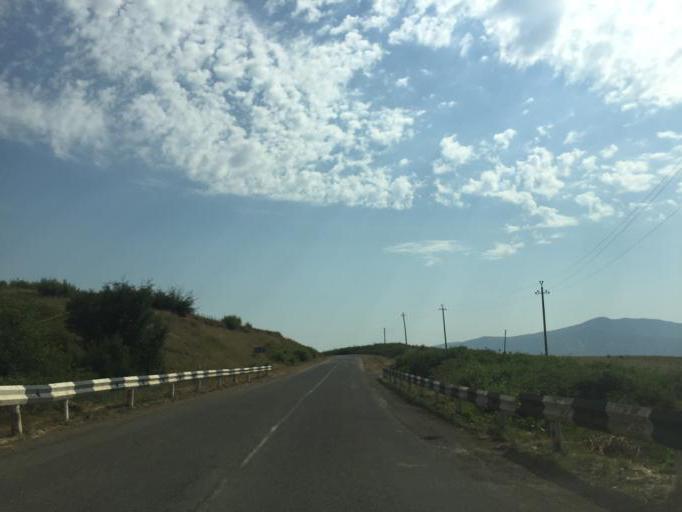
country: AZ
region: Xankandi Sahari
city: Xankandi
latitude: 39.8766
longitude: 46.7324
